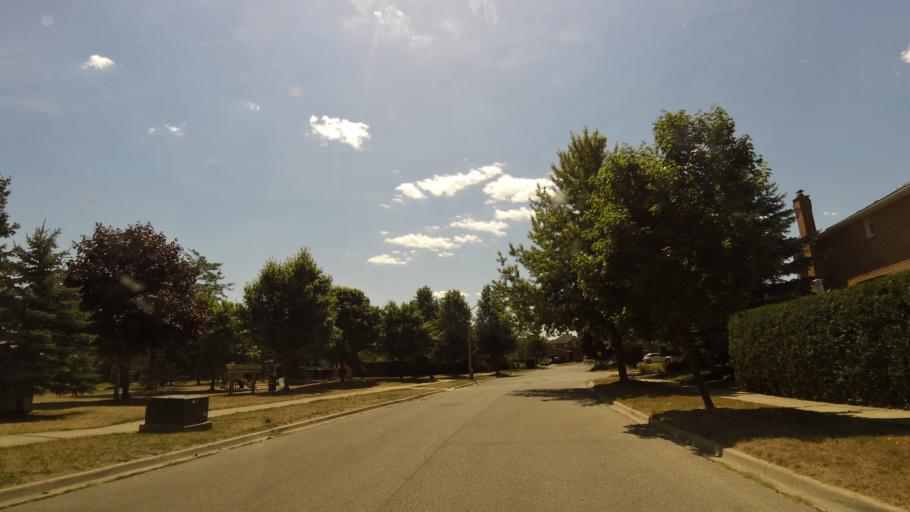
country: CA
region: Ontario
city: Brampton
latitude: 43.6401
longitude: -79.8715
